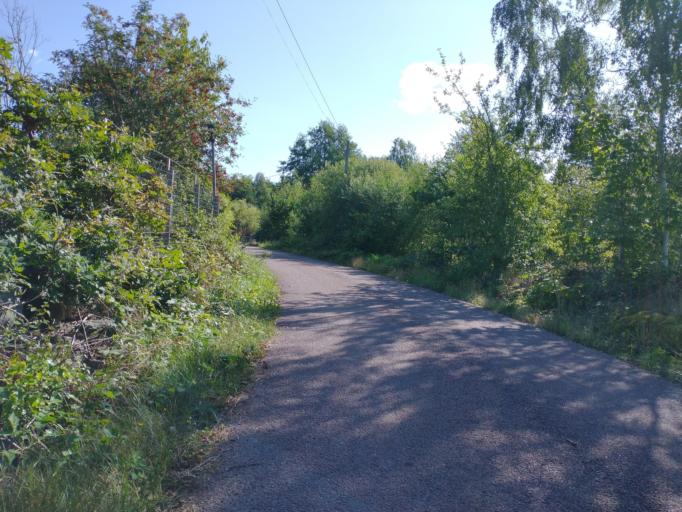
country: SE
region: Kalmar
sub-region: Kalmar Kommun
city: Lindsdal
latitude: 56.7944
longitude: 16.2633
